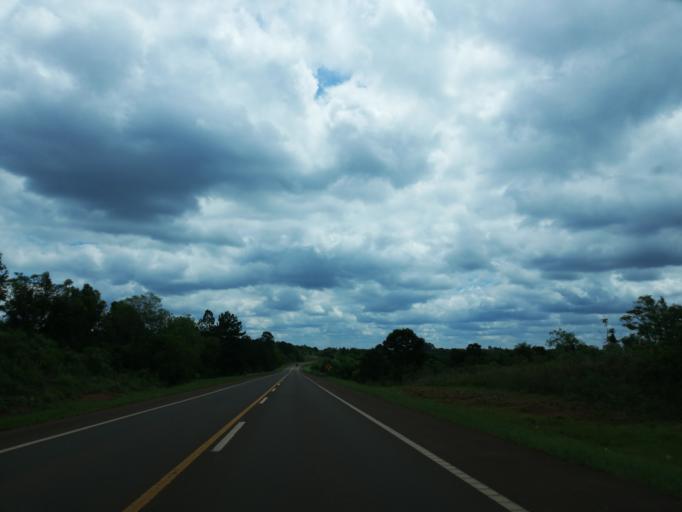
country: AR
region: Misiones
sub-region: Departamento de Leandro N. Alem
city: Leandro N. Alem
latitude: -27.6462
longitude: -55.3683
